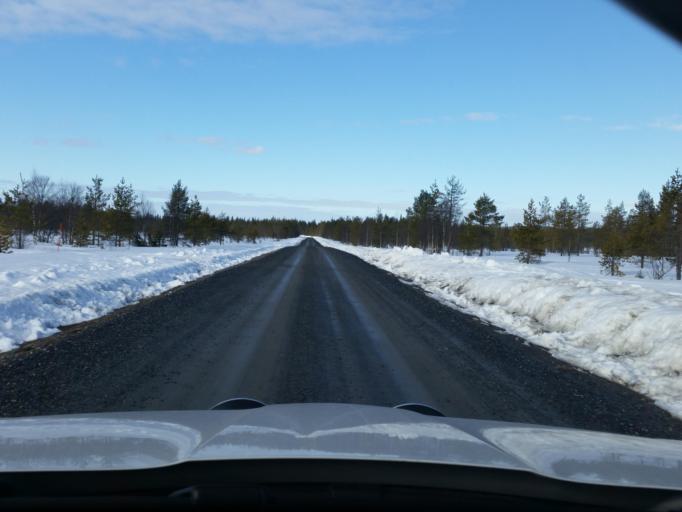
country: SE
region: Vaesterbotten
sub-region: Skelleftea Kommun
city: Storvik
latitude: 65.5165
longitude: 20.2383
